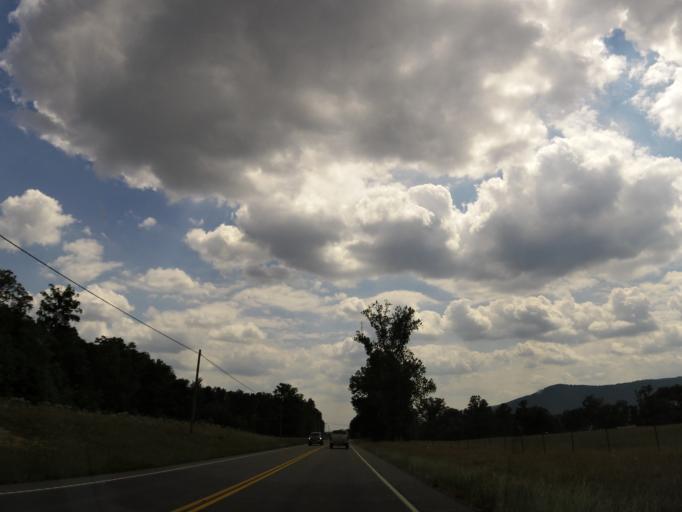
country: US
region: Tennessee
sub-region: Sequatchie County
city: Dunlap
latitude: 35.4217
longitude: -85.3591
